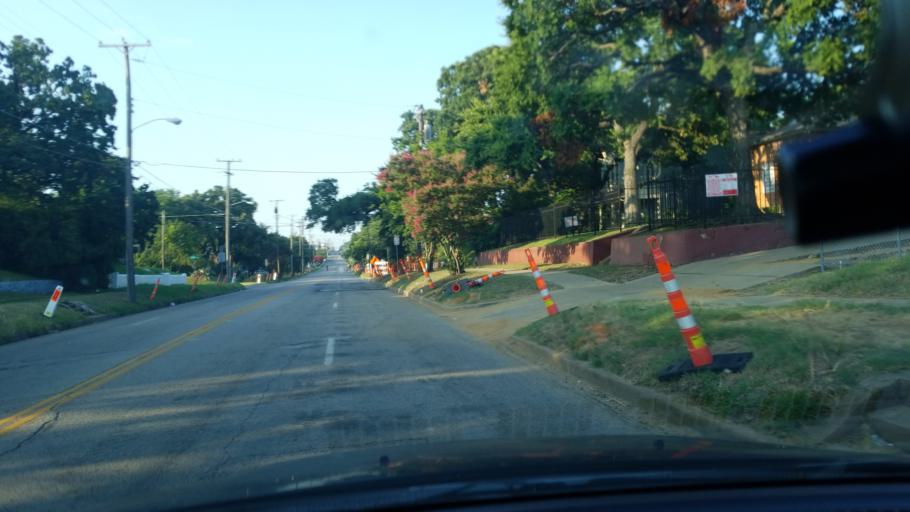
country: US
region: Texas
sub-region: Dallas County
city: Dallas
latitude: 32.7568
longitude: -96.8157
